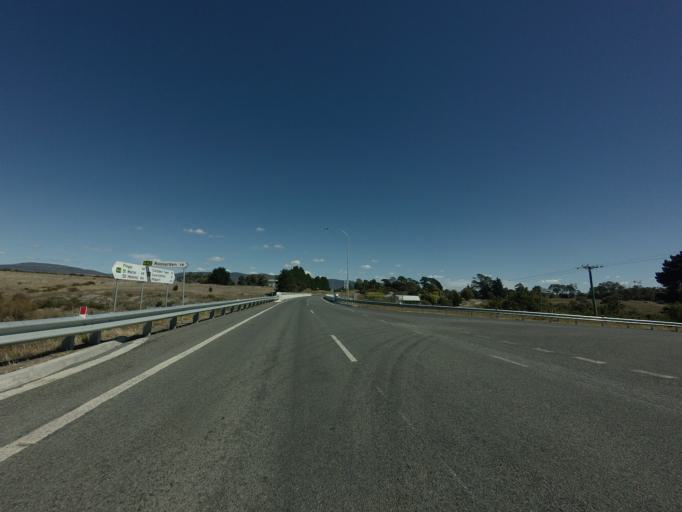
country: AU
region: Tasmania
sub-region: Northern Midlands
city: Evandale
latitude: -41.7832
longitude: 147.7195
